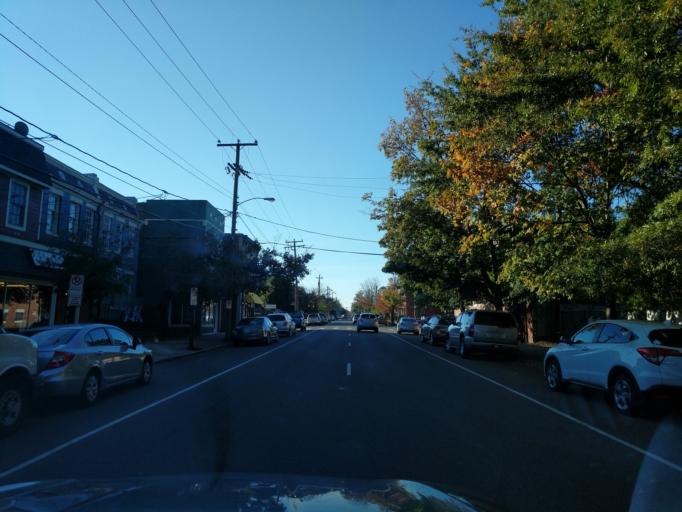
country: US
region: Virginia
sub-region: City of Richmond
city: Richmond
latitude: 37.5479
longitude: -77.4620
